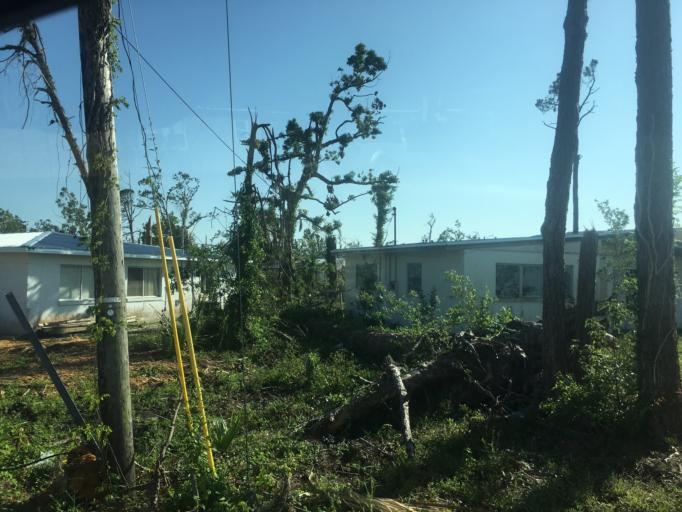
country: US
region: Florida
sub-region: Bay County
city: Panama City
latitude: 30.1476
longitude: -85.6485
